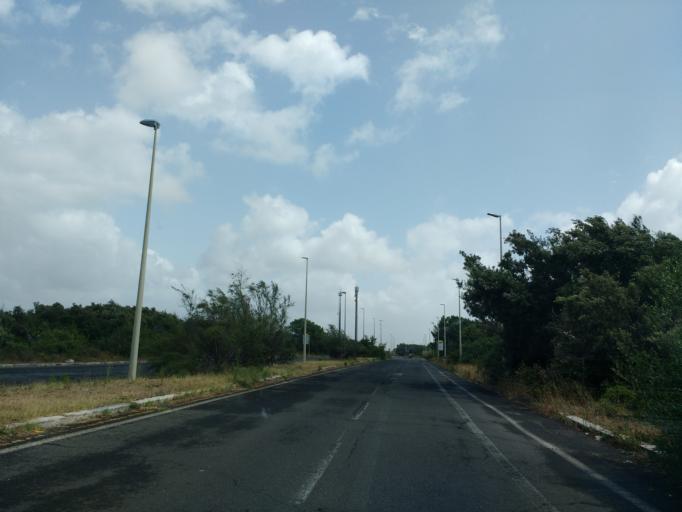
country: IT
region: Latium
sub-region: Citta metropolitana di Roma Capitale
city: Acilia-Castel Fusano-Ostia Antica
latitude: 41.7038
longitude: 12.3454
